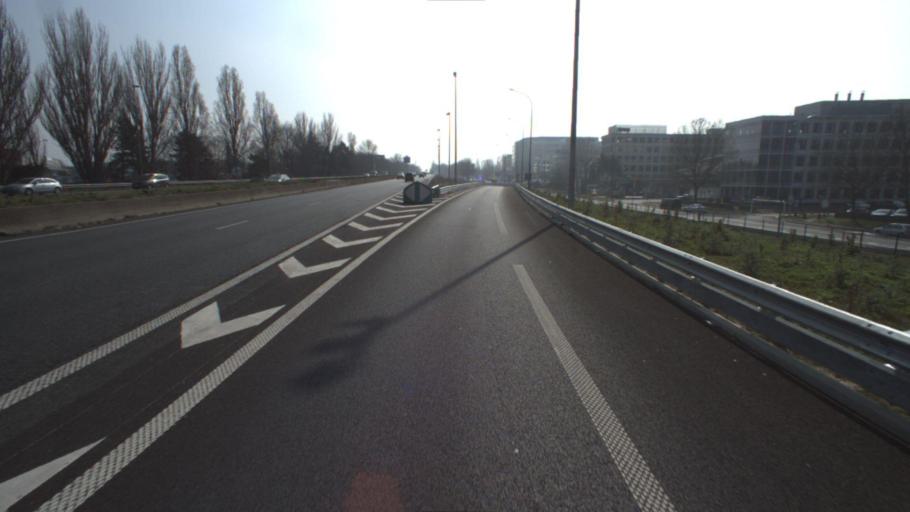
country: FR
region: Ile-de-France
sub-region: Departement du Val-de-Marne
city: Rungis
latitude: 48.7504
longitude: 2.3556
